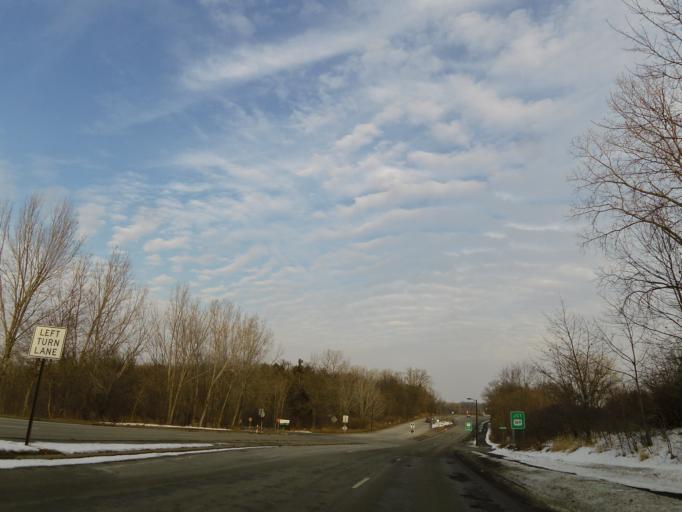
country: US
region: Minnesota
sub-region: Hennepin County
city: Eden Prairie
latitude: 44.8360
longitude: -93.4050
